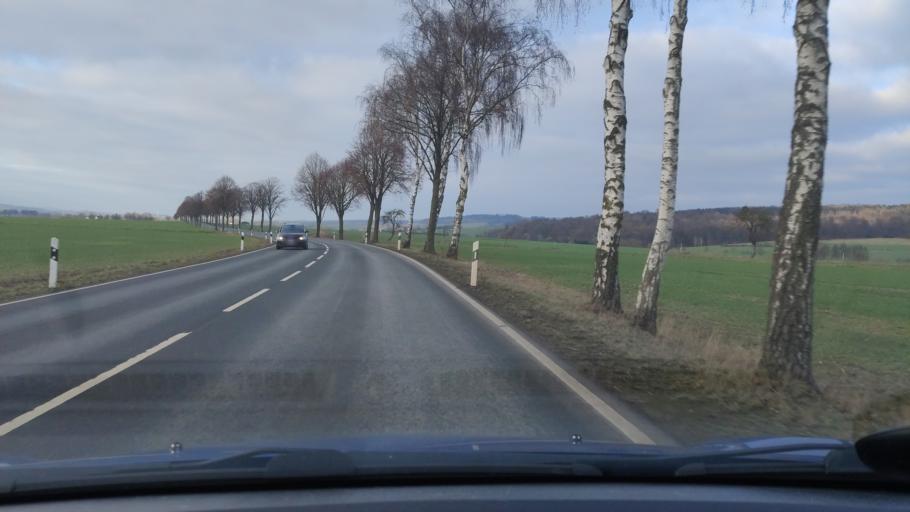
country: DE
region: Lower Saxony
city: Coppenbrugge
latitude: 52.1421
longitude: 9.5142
